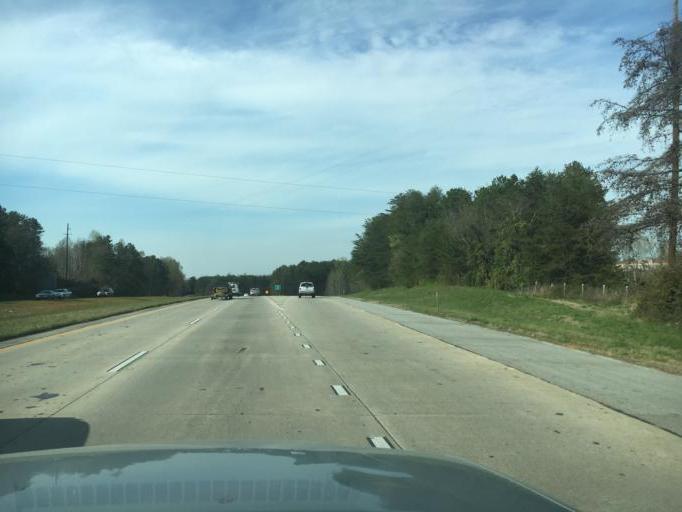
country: US
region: Georgia
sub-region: Habersham County
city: Cornelia
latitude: 34.5320
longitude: -83.5406
